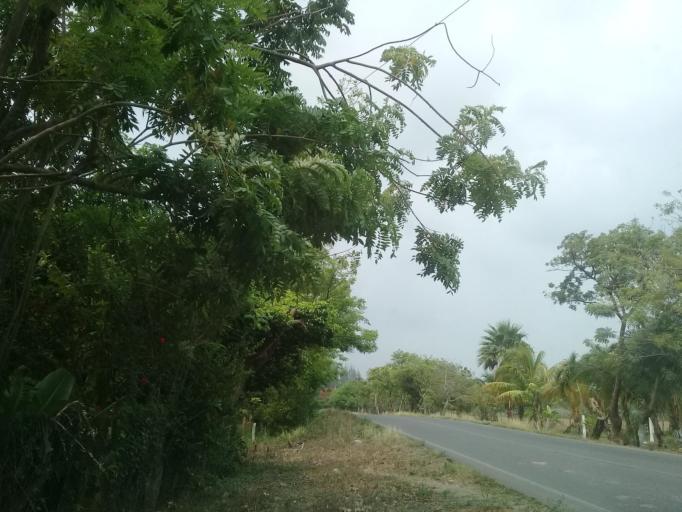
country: MX
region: Veracruz
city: Jamapa
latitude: 19.0523
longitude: -96.2043
